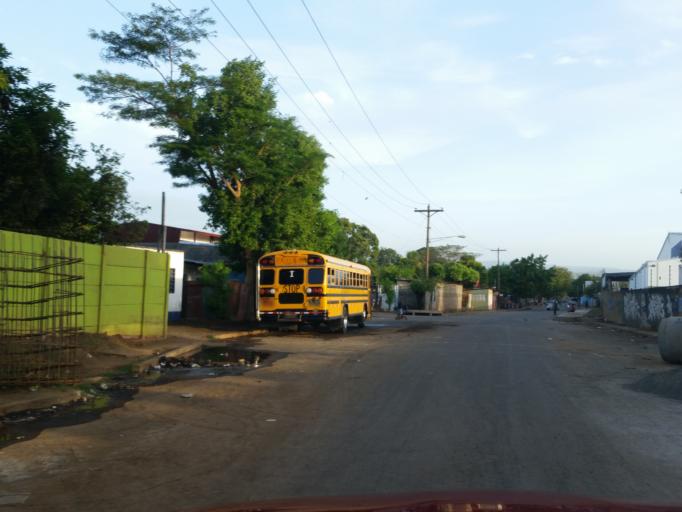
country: NI
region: Managua
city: Managua
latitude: 12.1357
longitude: -86.2775
